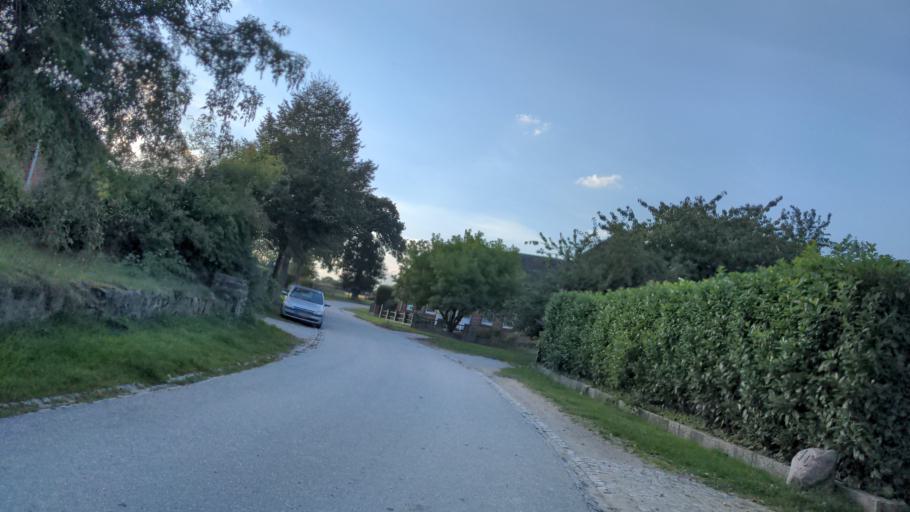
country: DE
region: Schleswig-Holstein
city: Ahrensbok
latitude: 53.9804
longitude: 10.6283
